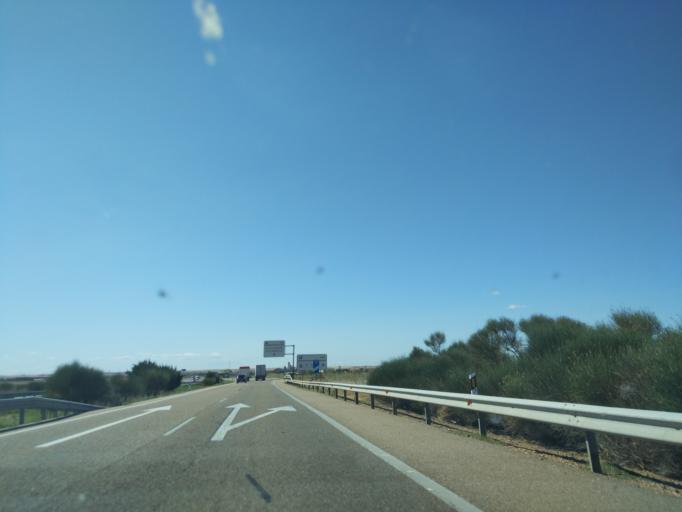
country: ES
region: Castille and Leon
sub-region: Provincia de Zamora
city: Villalpando
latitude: 41.8480
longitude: -5.4007
